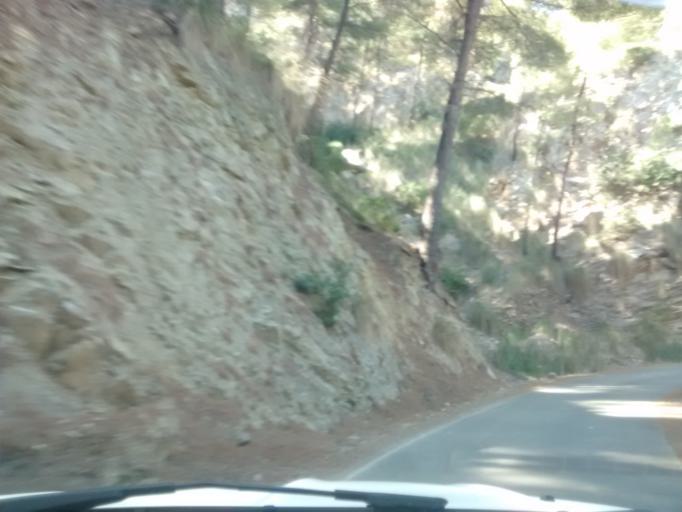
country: ES
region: Balearic Islands
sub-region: Illes Balears
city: Port d'Alcudia
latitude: 39.8774
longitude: 3.1754
